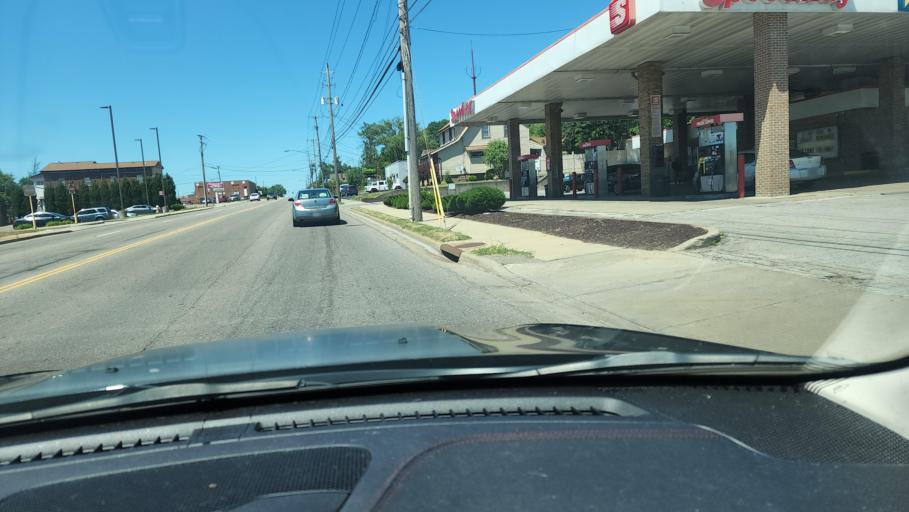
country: US
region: Ohio
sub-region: Trumbull County
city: Girard
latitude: 41.1032
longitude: -80.7110
